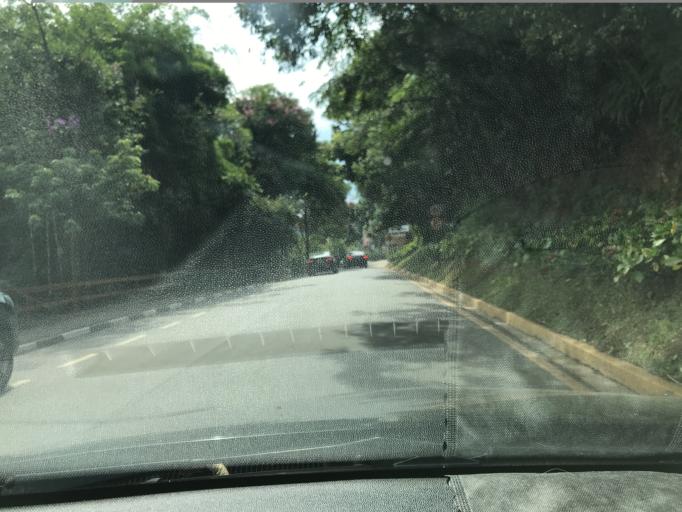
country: BR
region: Sao Paulo
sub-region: Campos Do Jordao
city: Campos do Jordao
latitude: -22.8250
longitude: -45.6653
